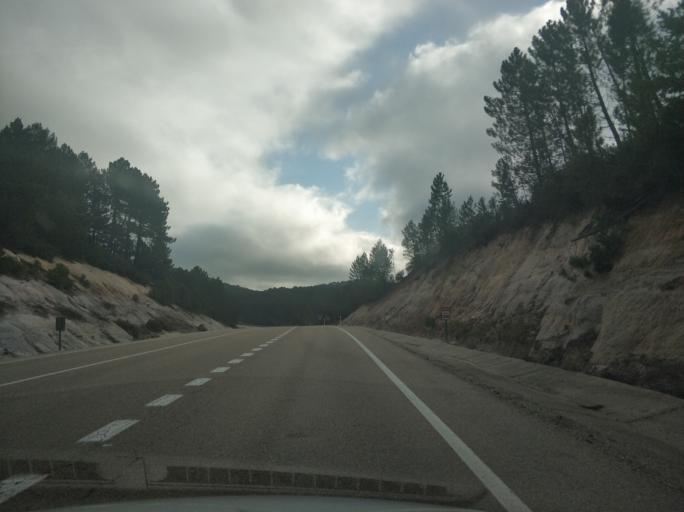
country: ES
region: Castille and Leon
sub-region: Provincia de Soria
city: Navaleno
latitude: 41.8303
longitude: -2.9778
